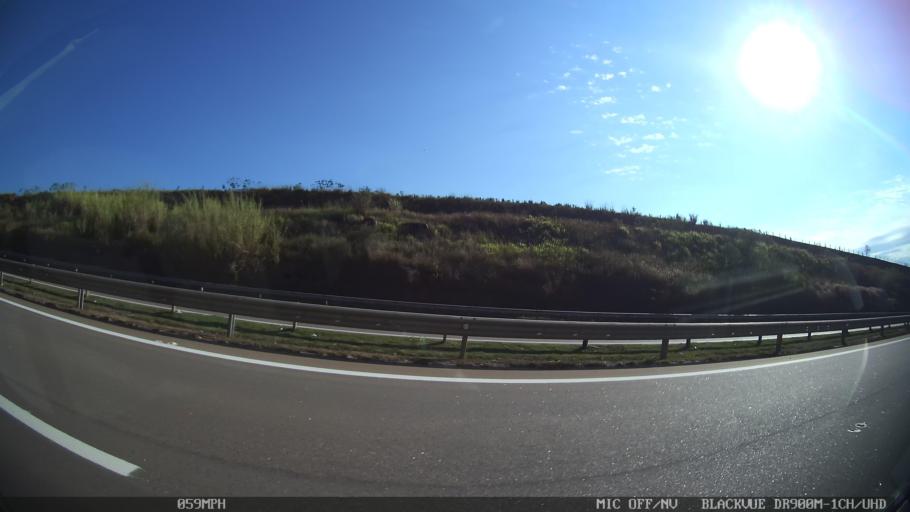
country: BR
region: Sao Paulo
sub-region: Piracicaba
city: Piracicaba
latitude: -22.7089
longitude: -47.6114
